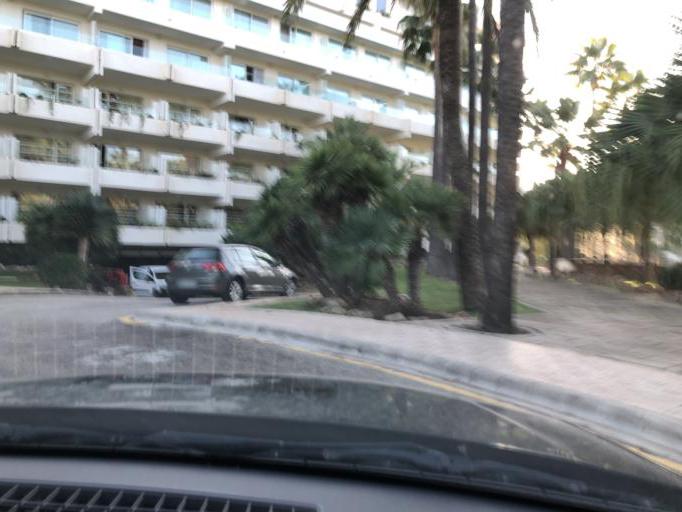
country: ES
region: Balearic Islands
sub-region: Illes Balears
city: Santa Ponsa
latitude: 39.5354
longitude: 2.4606
